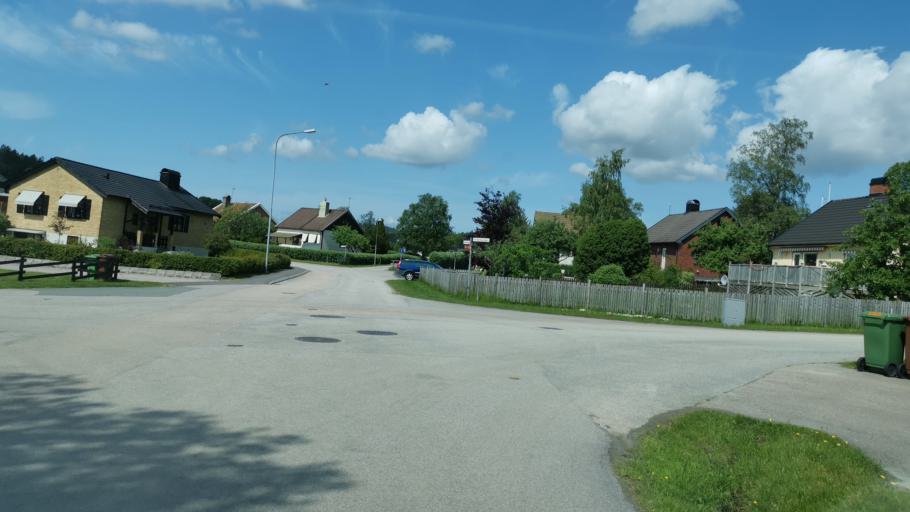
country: SE
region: Vaestra Goetaland
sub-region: Uddevalla Kommun
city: Uddevalla
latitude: 58.3534
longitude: 11.8429
